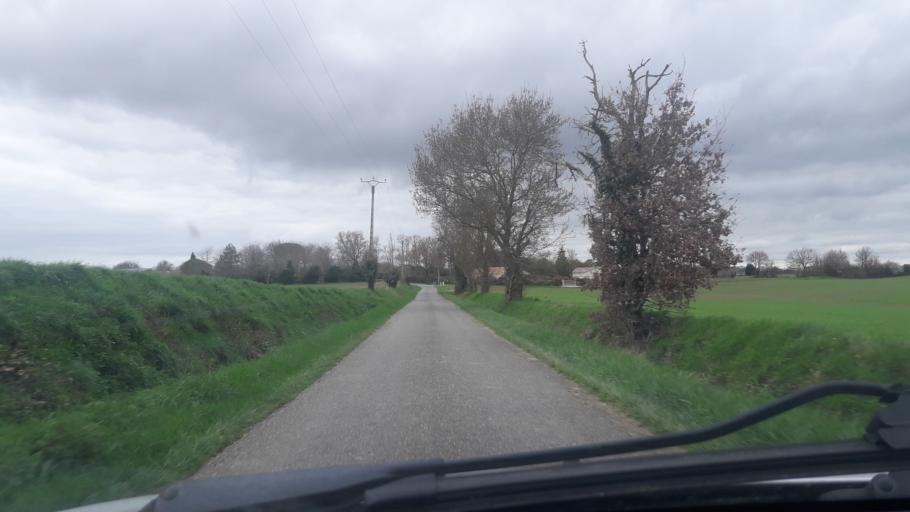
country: FR
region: Midi-Pyrenees
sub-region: Departement du Gers
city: Gimont
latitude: 43.6520
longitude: 1.0132
